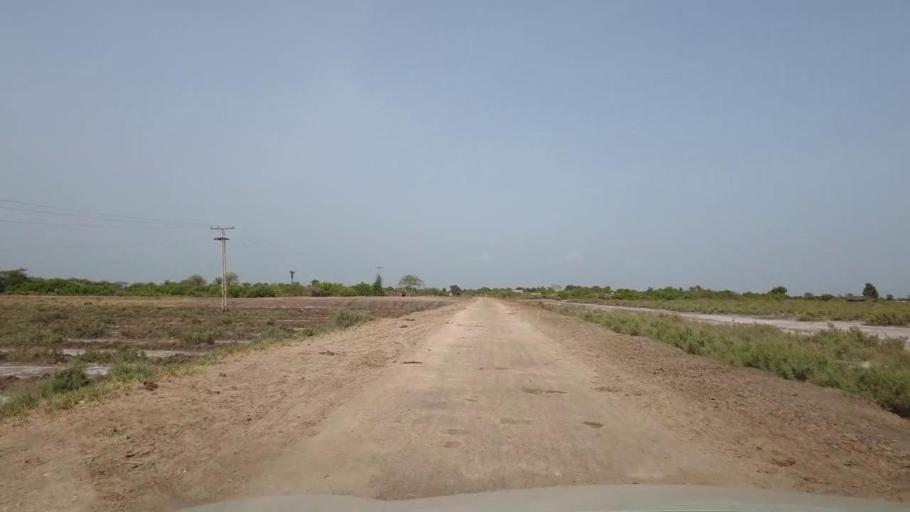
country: PK
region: Sindh
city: Mirwah Gorchani
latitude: 25.2763
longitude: 68.9683
